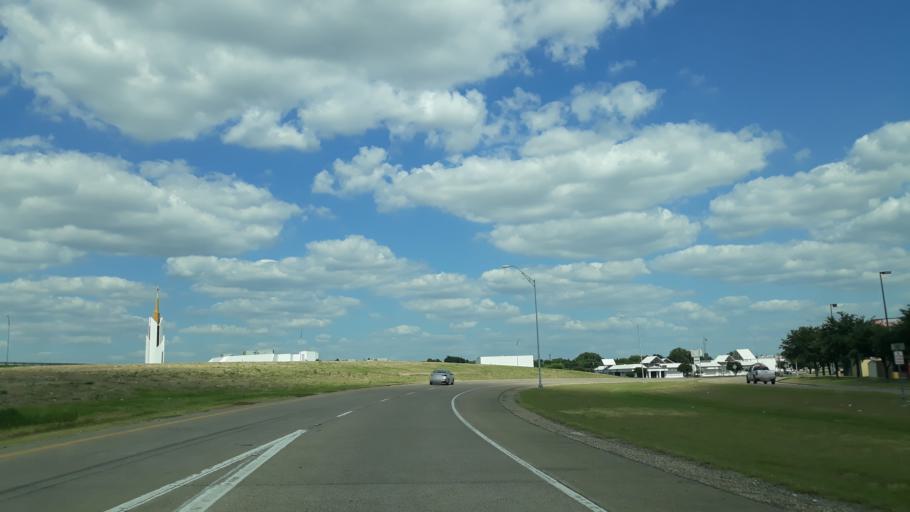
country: US
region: Texas
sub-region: Dallas County
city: Irving
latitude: 32.8351
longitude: -96.9911
